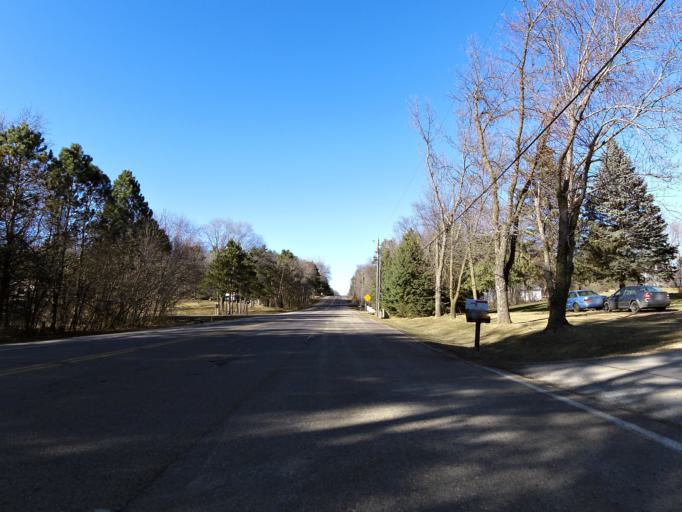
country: US
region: Minnesota
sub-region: Washington County
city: Bayport
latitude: 44.9791
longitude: -92.8223
